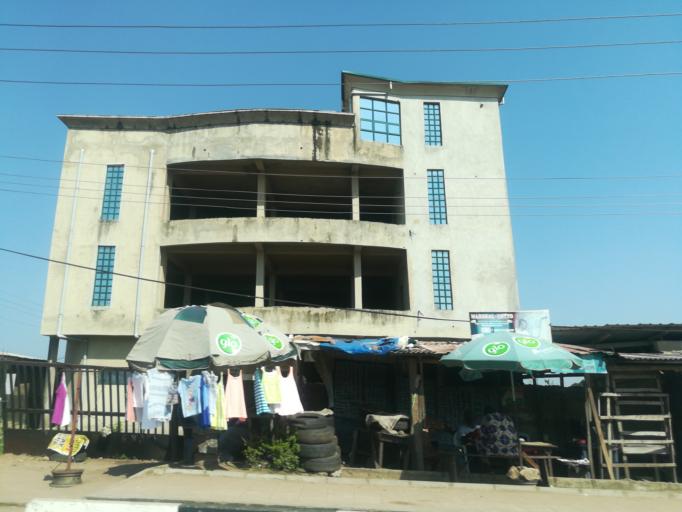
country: NG
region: Ogun
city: Abeokuta
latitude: 7.1407
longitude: 3.3309
